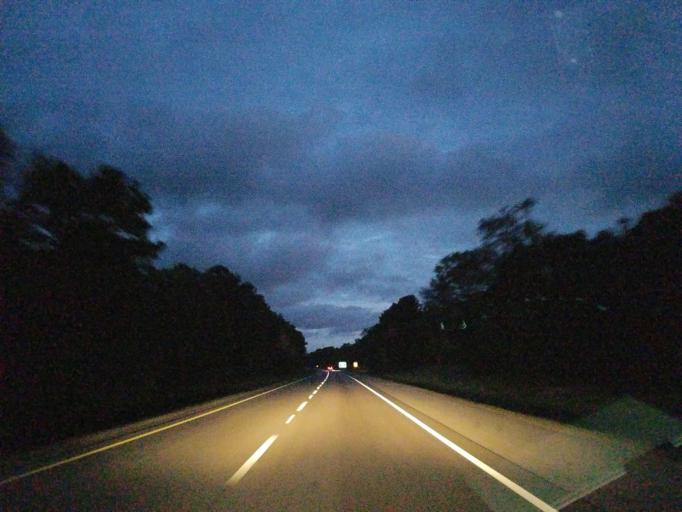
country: US
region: Mississippi
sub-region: Jones County
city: Sharon
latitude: 31.8559
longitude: -89.0484
